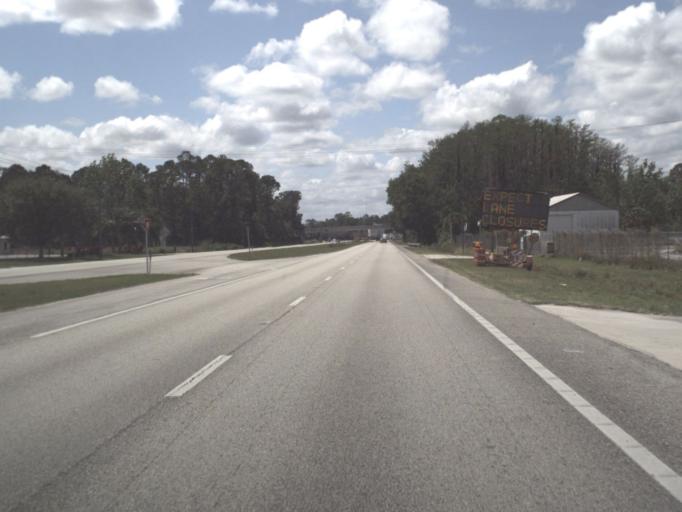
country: US
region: Florida
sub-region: Flagler County
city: Bunnell
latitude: 29.4786
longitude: -81.2675
